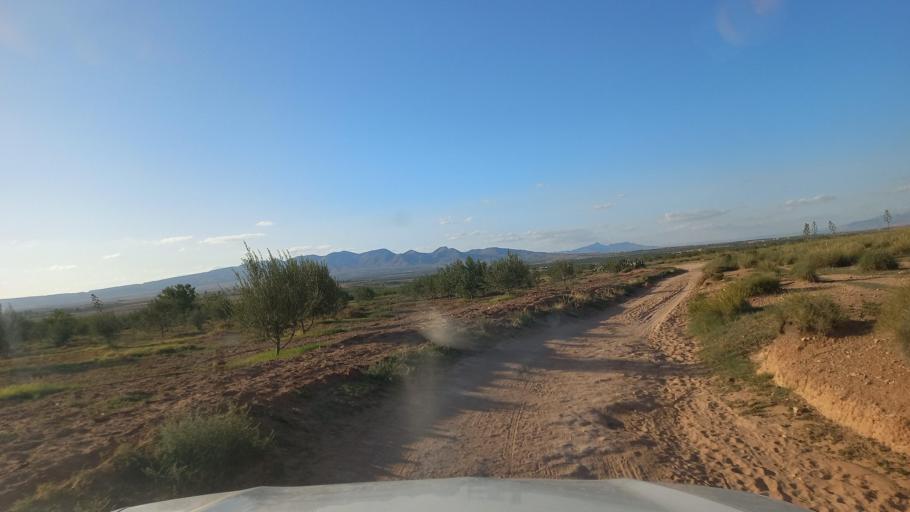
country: TN
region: Al Qasrayn
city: Sbiba
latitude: 35.3871
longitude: 9.1545
